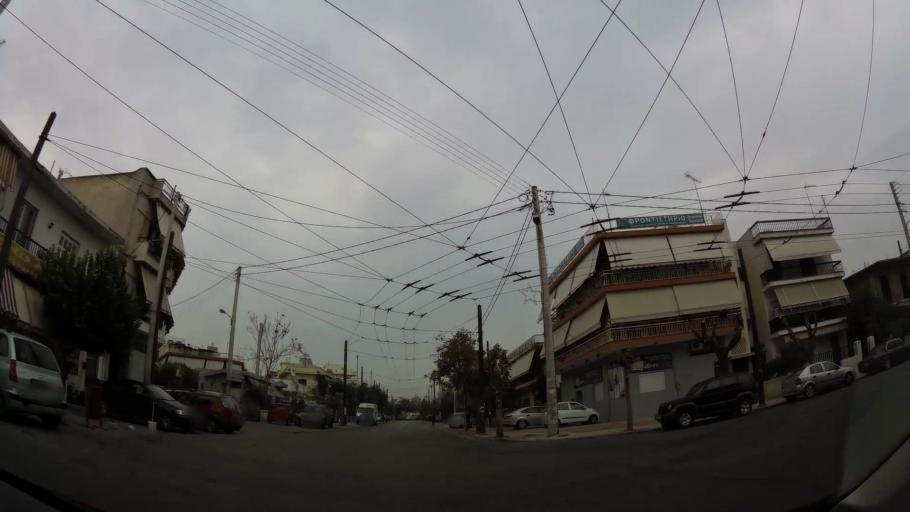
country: GR
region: Attica
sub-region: Nomarchia Athinas
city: Peristeri
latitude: 38.0095
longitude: 23.7019
